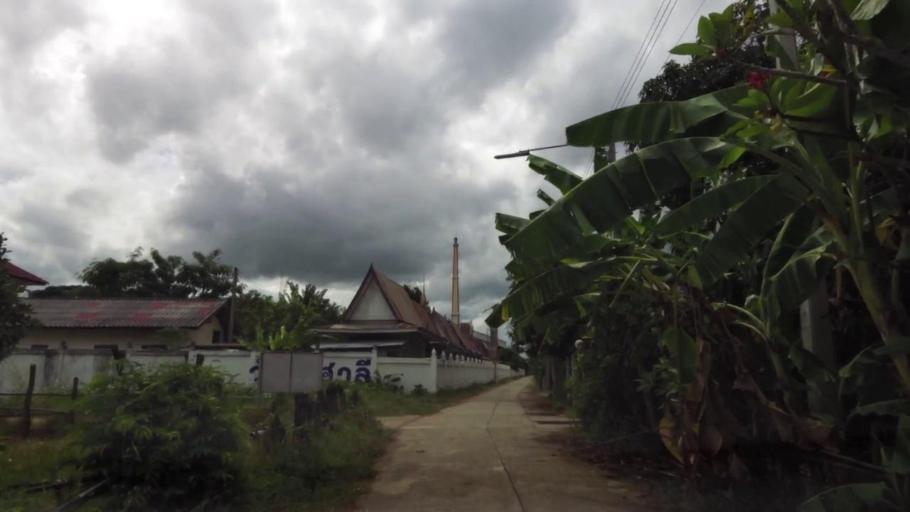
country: TH
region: Nakhon Sawan
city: Phai Sali
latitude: 15.6022
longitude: 100.6518
